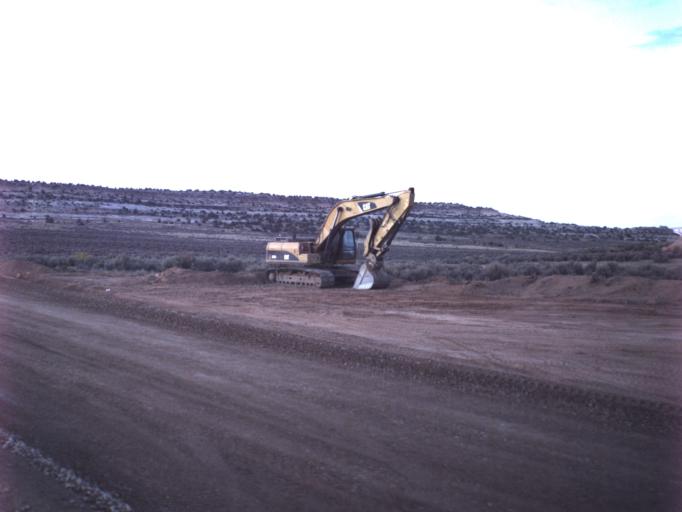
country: US
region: Utah
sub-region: San Juan County
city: Monticello
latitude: 38.0895
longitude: -109.3562
